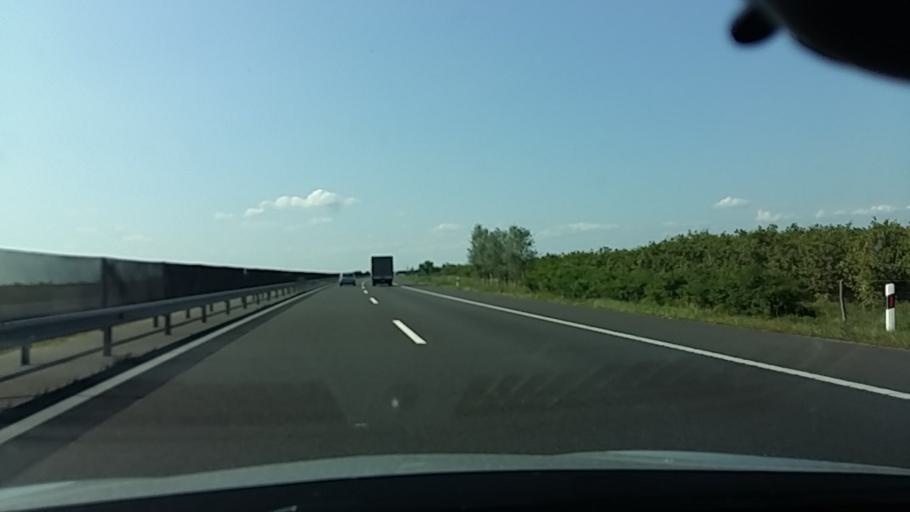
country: HU
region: Hajdu-Bihar
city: Polgar
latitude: 47.8117
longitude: 21.1600
